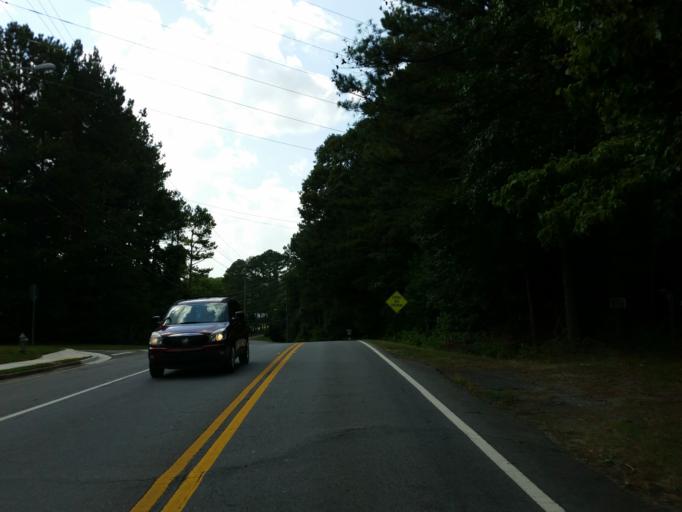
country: US
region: Georgia
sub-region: Cherokee County
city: Woodstock
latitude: 34.0470
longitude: -84.4937
